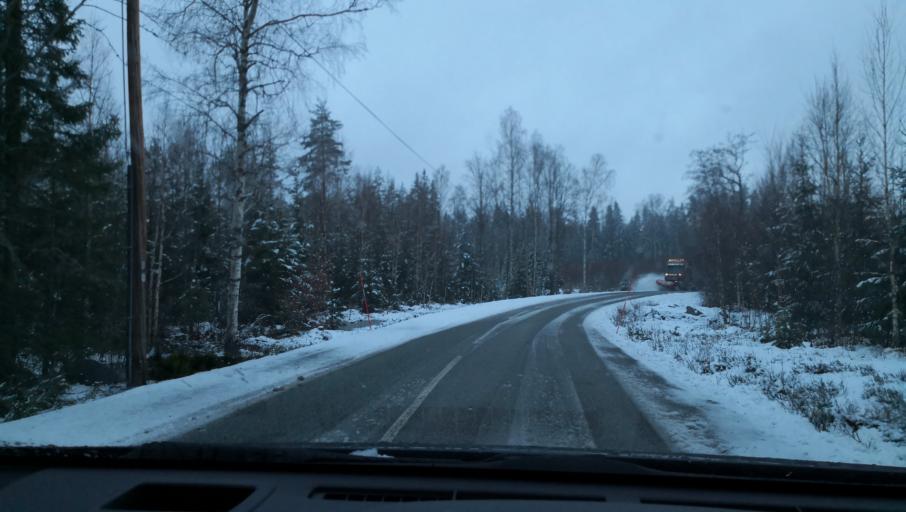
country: SE
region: Vaestmanland
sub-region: Kopings Kommun
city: Kolsva
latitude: 59.5716
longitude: 15.7976
